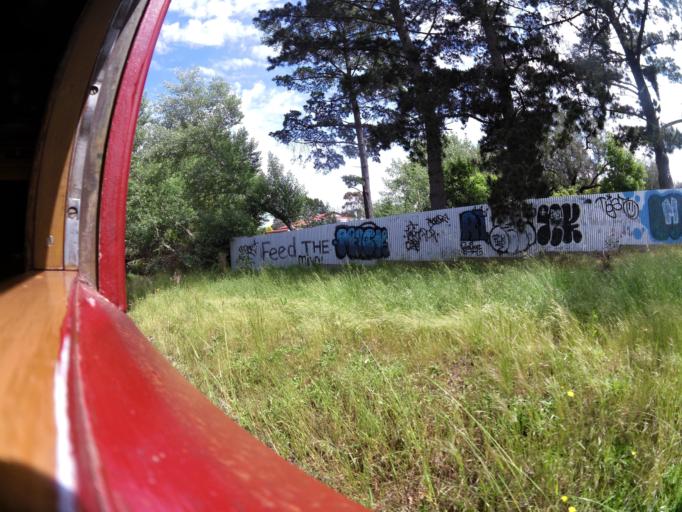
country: AU
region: Victoria
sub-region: Mount Alexander
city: Castlemaine
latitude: -37.0725
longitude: 144.2140
